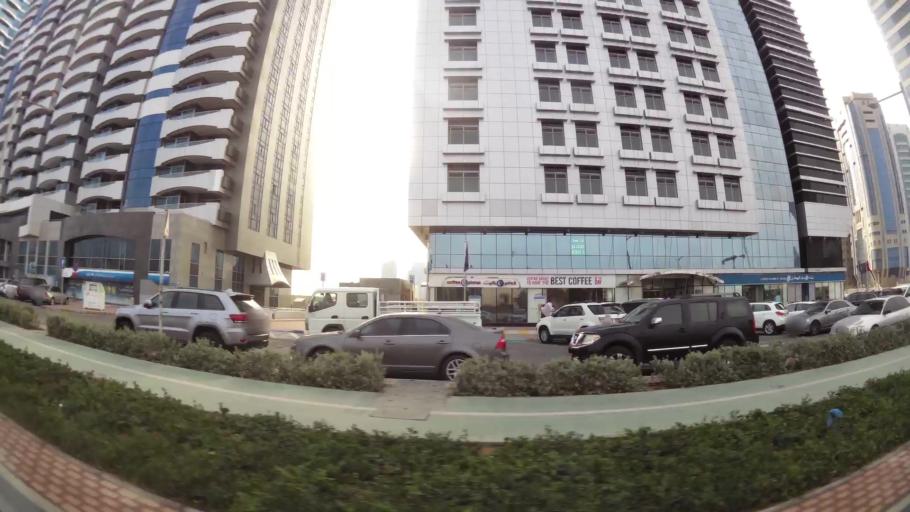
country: AE
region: Abu Dhabi
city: Abu Dhabi
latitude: 24.5061
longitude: 54.3752
